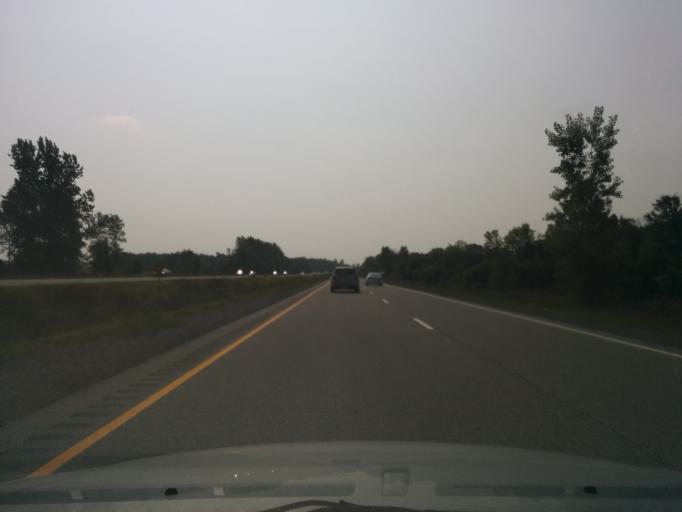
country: CA
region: Ontario
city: Bells Corners
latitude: 45.1399
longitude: -75.6781
